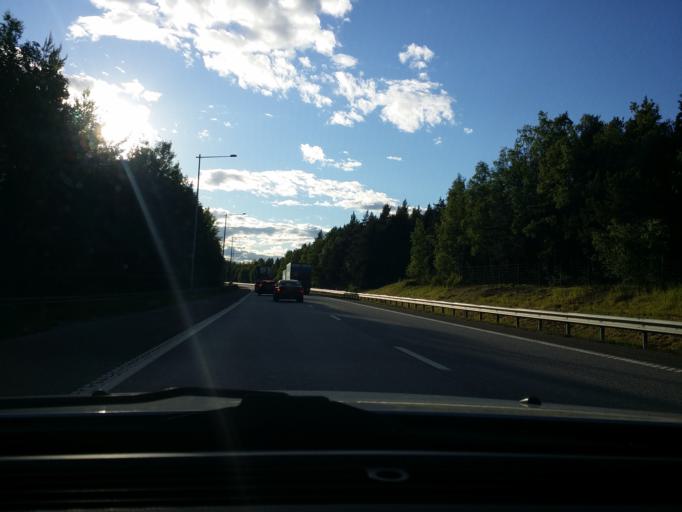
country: SE
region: Stockholm
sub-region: Upplands-Bro Kommun
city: Bro
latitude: 59.5215
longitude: 17.6622
